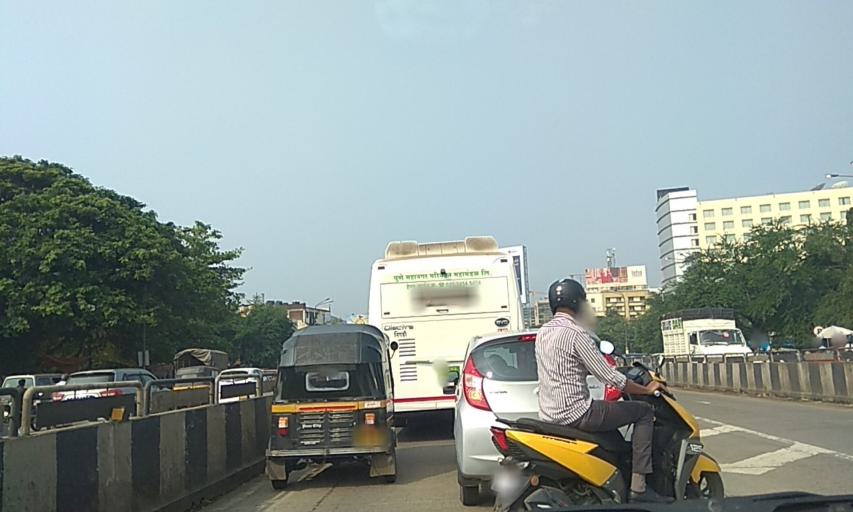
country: IN
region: Maharashtra
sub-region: Pune Division
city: Lohogaon
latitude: 18.5624
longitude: 73.9239
